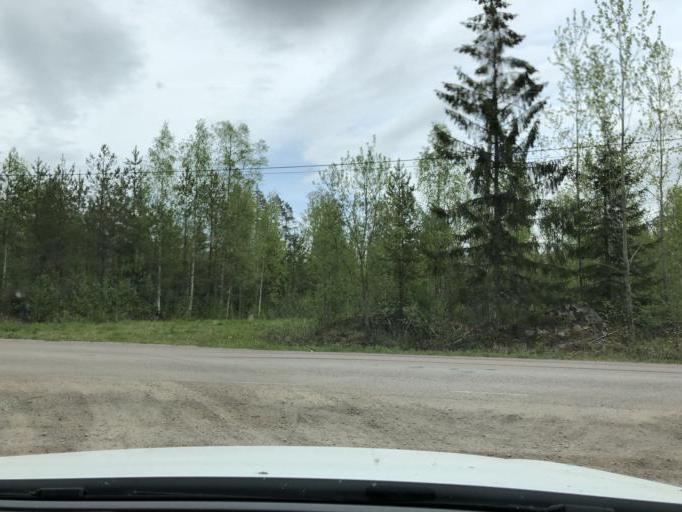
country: SE
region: Uppsala
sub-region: Heby Kommun
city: OEstervala
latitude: 60.3735
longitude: 17.2408
